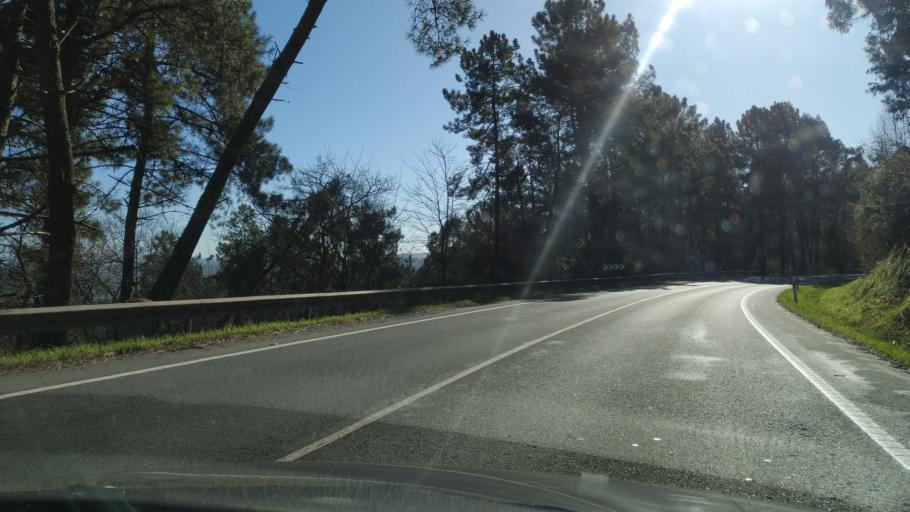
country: ES
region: Galicia
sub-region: Provincia da Coruna
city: Ribeira
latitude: 42.7458
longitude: -8.3392
